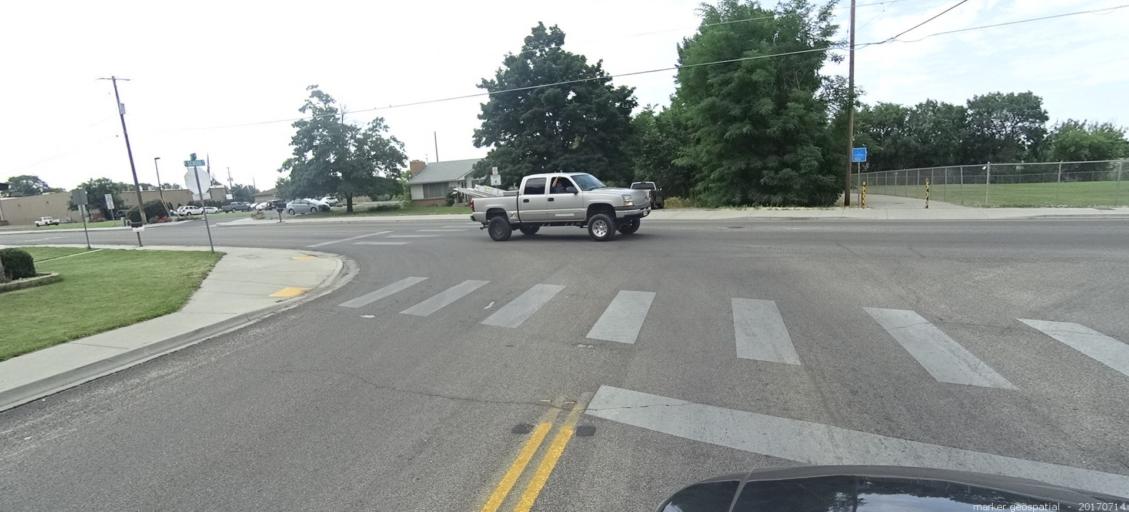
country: US
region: Idaho
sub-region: Ada County
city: Kuna
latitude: 43.4922
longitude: -116.4237
